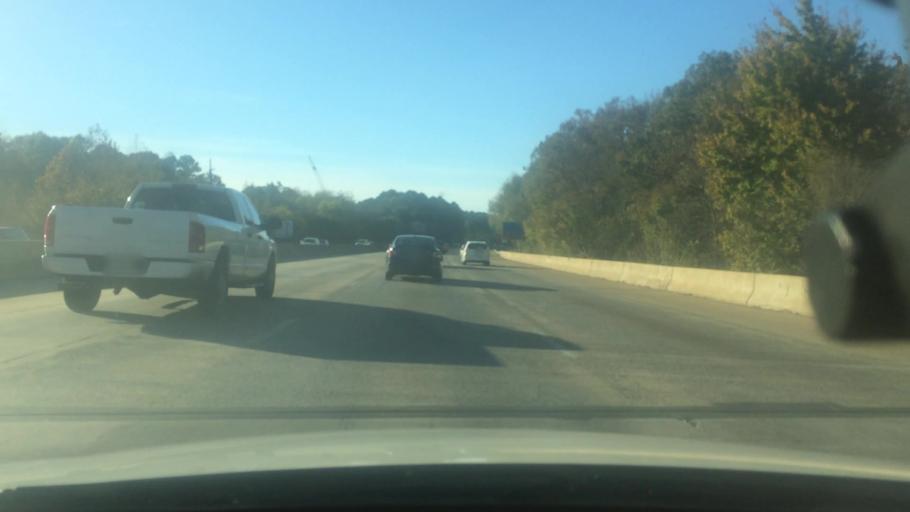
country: US
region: North Carolina
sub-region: Orange County
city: Chapel Hill
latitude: 35.9046
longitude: -78.9697
